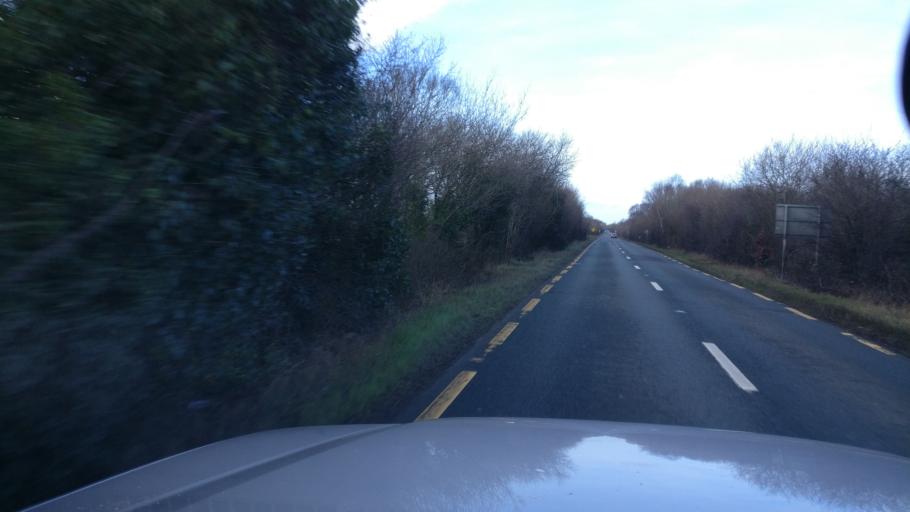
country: IE
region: Leinster
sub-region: Laois
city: Mountmellick
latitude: 53.0711
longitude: -7.3284
